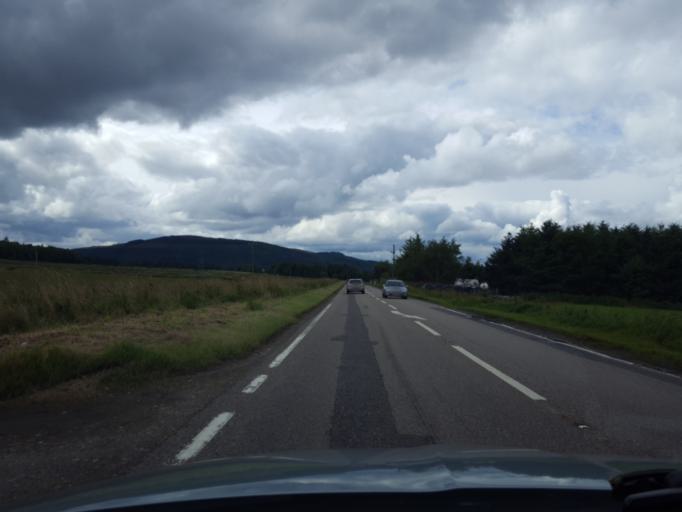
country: GB
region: Scotland
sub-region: Moray
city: Rothes
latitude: 57.4284
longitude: -3.3447
